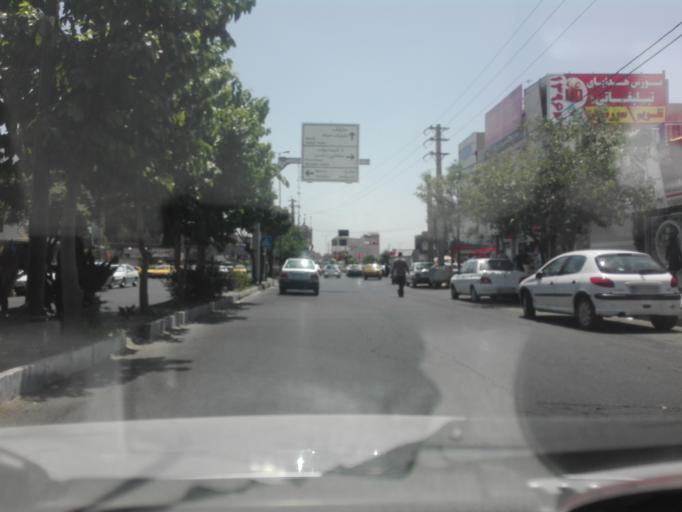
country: IR
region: Tehran
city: Malard
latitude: 35.7111
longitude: 50.9847
